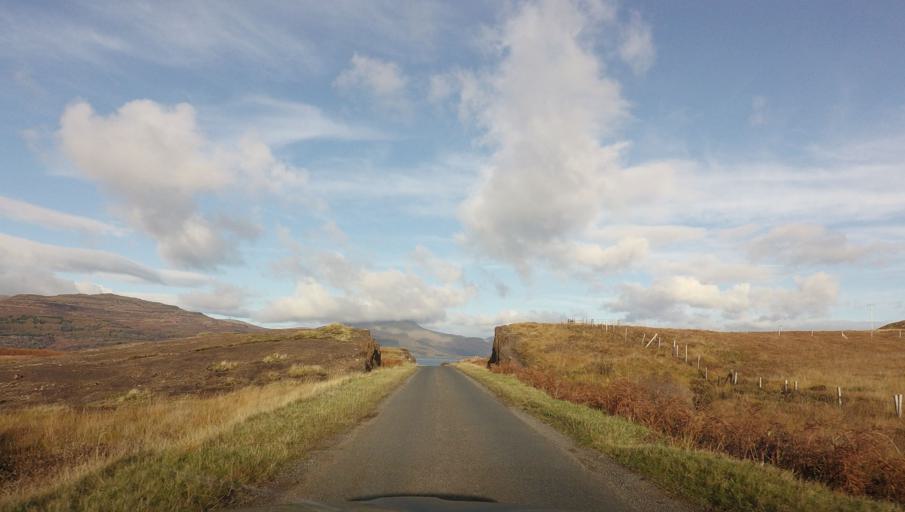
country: GB
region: Scotland
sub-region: Argyll and Bute
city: Isle Of Mull
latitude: 56.3415
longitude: -6.1249
